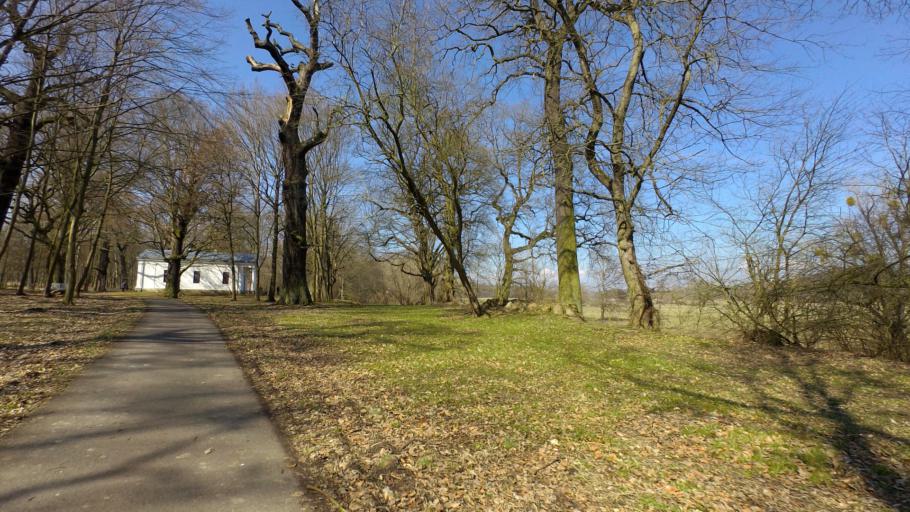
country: DE
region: Saxony-Anhalt
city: Vockerode
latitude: 51.8662
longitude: 12.3225
